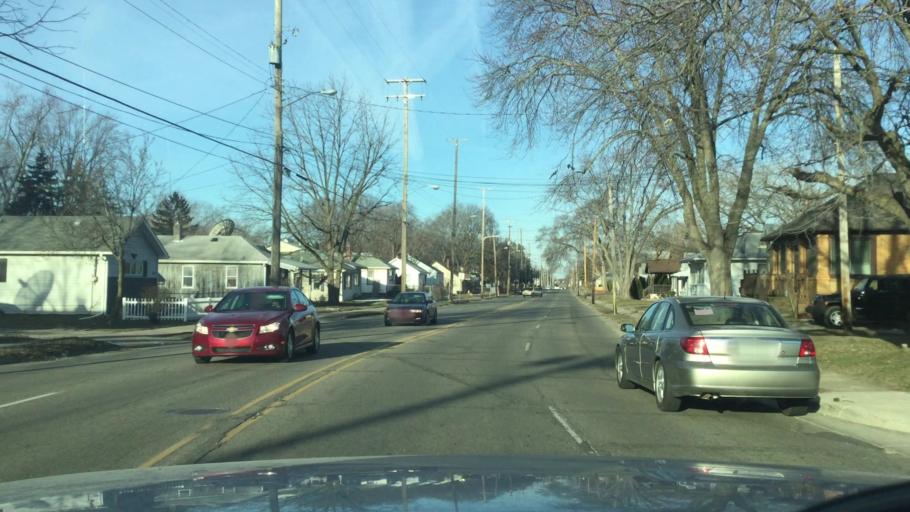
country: US
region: Michigan
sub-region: Genesee County
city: Flint
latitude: 42.9884
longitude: -83.6940
